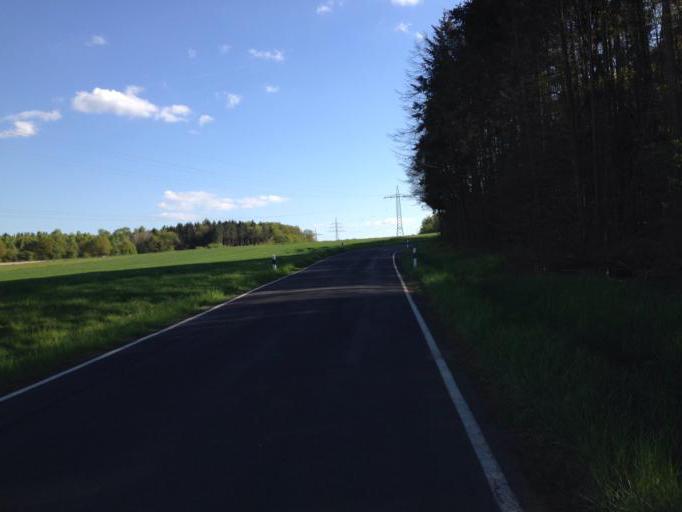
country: DE
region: Hesse
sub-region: Regierungsbezirk Giessen
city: Grossen Buseck
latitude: 50.5736
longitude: 8.7989
